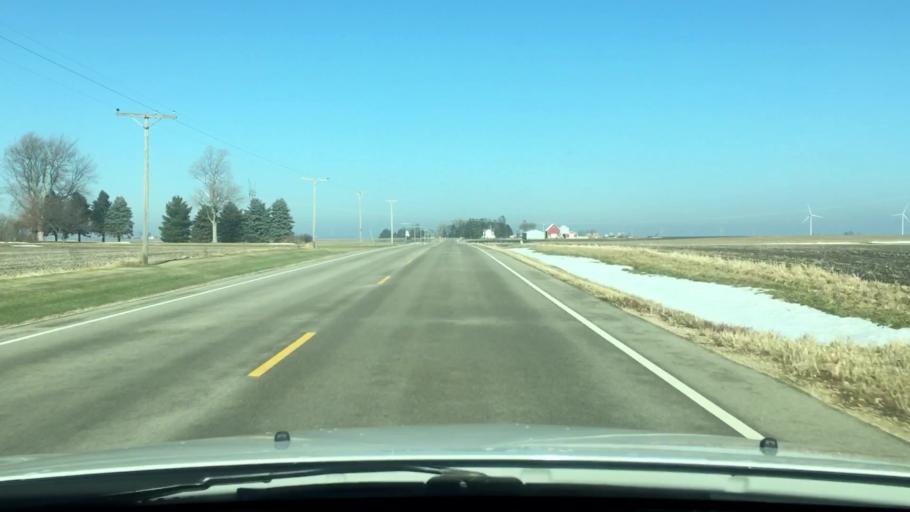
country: US
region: Illinois
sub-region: DeKalb County
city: Waterman
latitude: 41.7973
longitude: -88.8871
